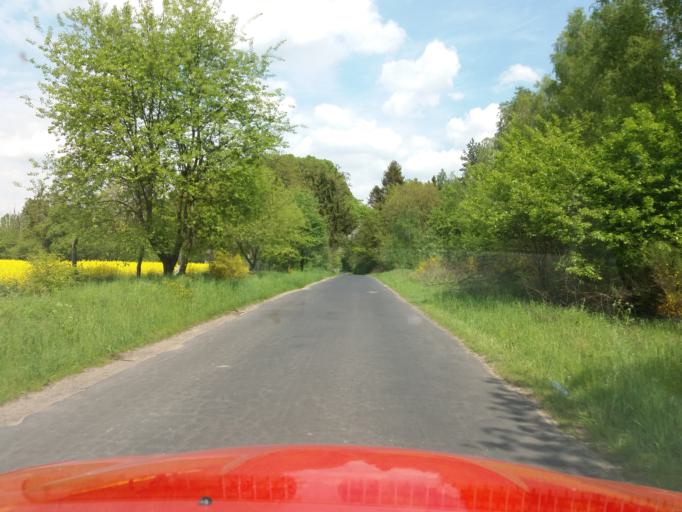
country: PL
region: West Pomeranian Voivodeship
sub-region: Powiat choszczenski
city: Bierzwnik
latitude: 53.1206
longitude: 15.6501
